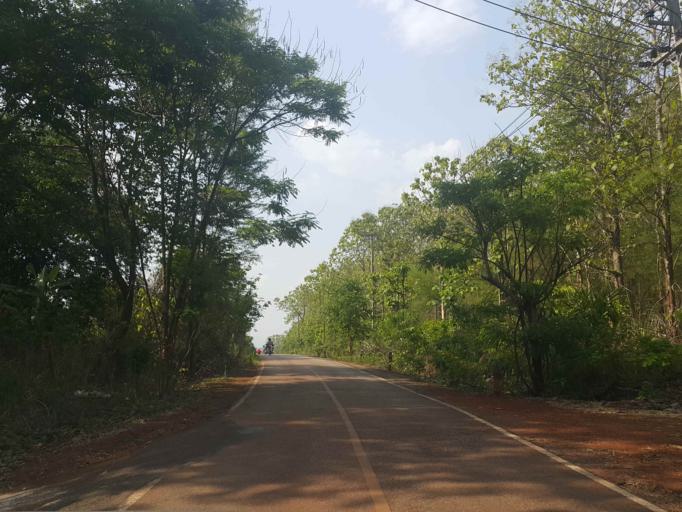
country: TH
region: Chiang Mai
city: Mae Taeng
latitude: 19.0793
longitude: 99.0870
